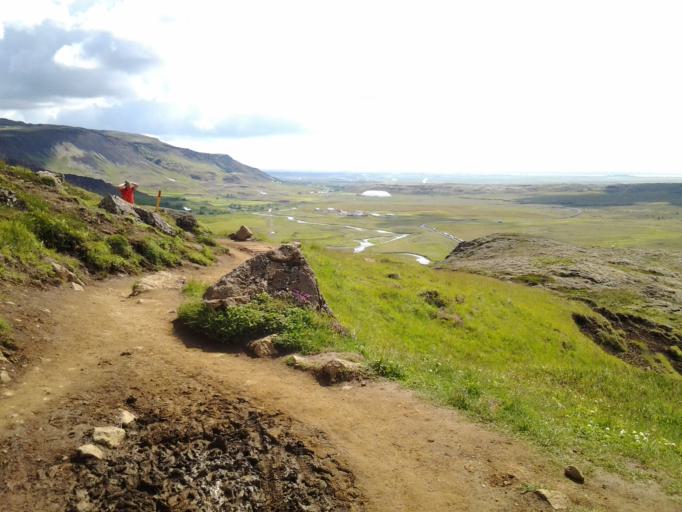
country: IS
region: South
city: Hveragerdi
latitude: 64.0282
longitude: -21.2163
